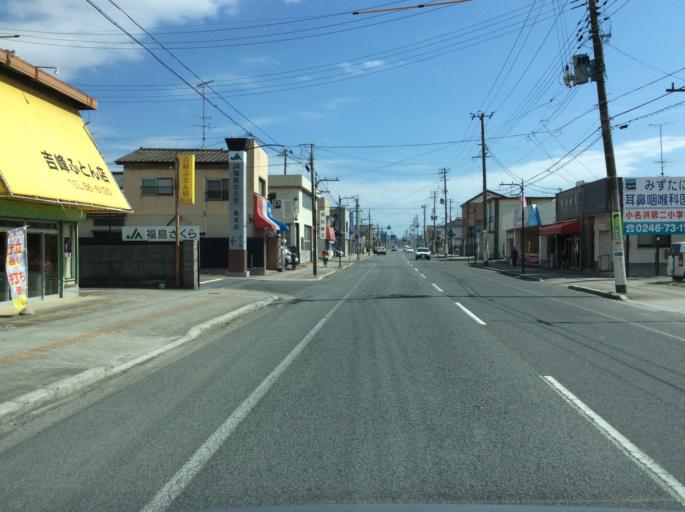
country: JP
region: Fukushima
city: Iwaki
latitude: 36.9550
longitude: 140.8559
